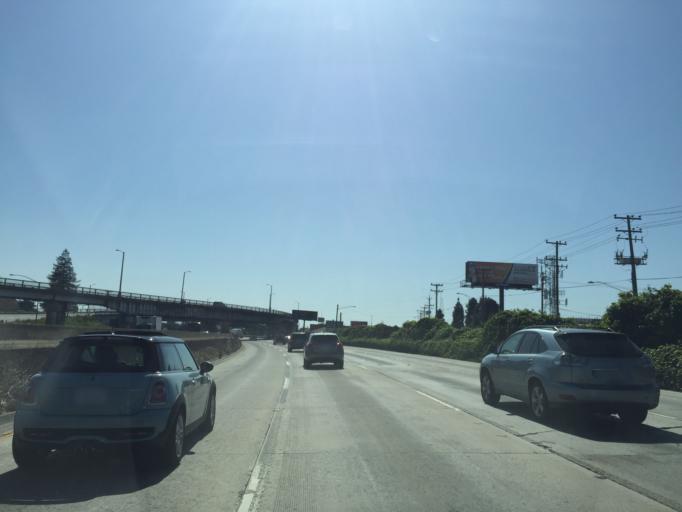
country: US
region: California
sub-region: Alameda County
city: Alameda
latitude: 37.7793
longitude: -122.2381
